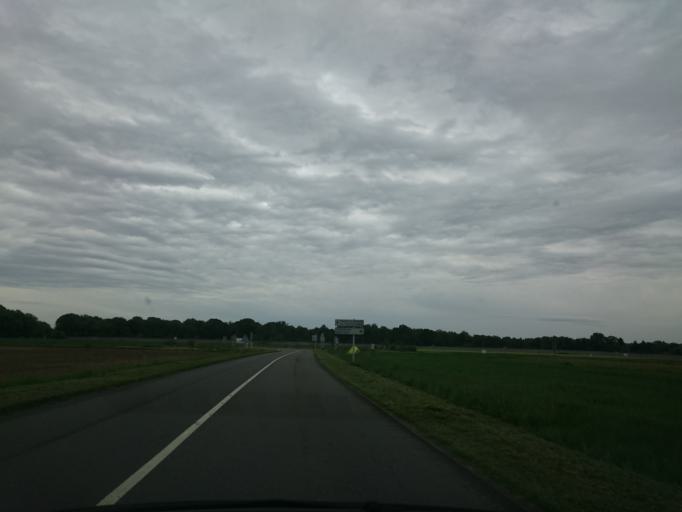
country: FR
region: Centre
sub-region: Departement du Loir-et-Cher
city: Muides-sur-Loire
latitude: 47.6618
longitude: 1.5348
